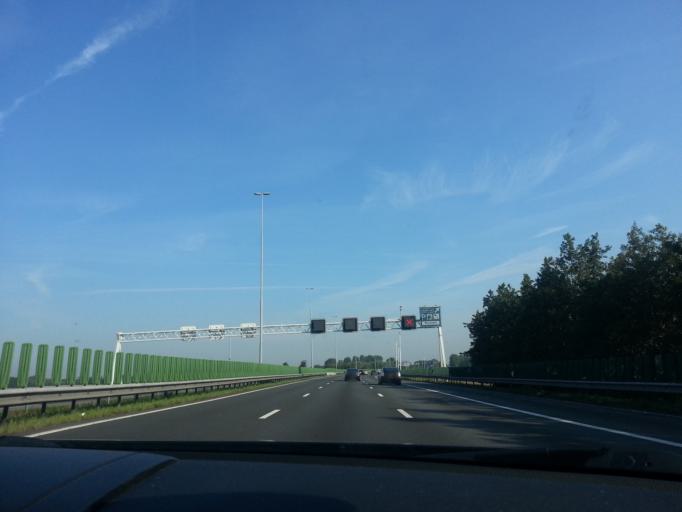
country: NL
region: South Holland
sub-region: Gemeente Schiedam
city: Schiedam
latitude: 51.9696
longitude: 4.4012
